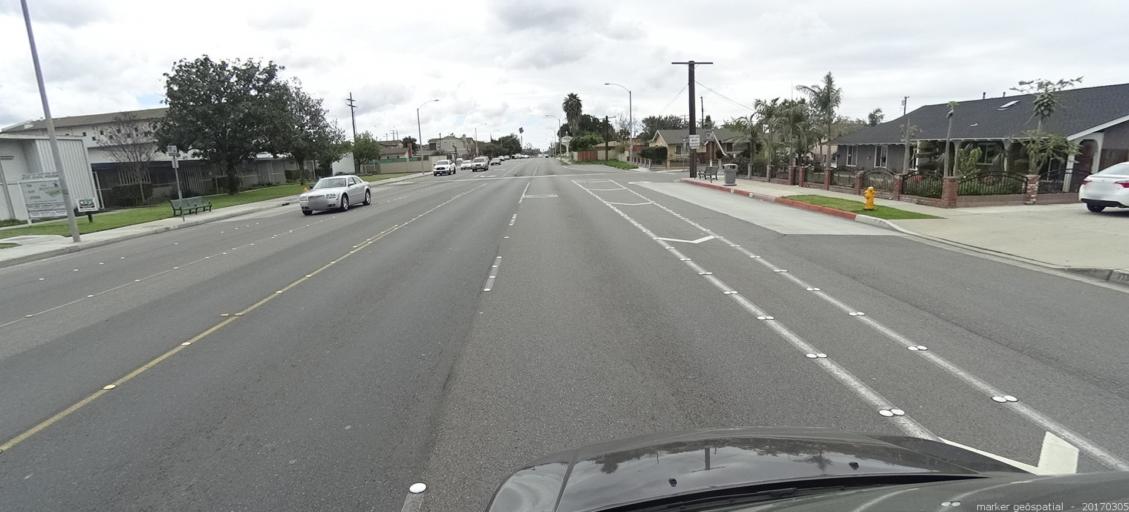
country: US
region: California
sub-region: Orange County
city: Stanton
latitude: 33.8221
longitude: -117.9760
